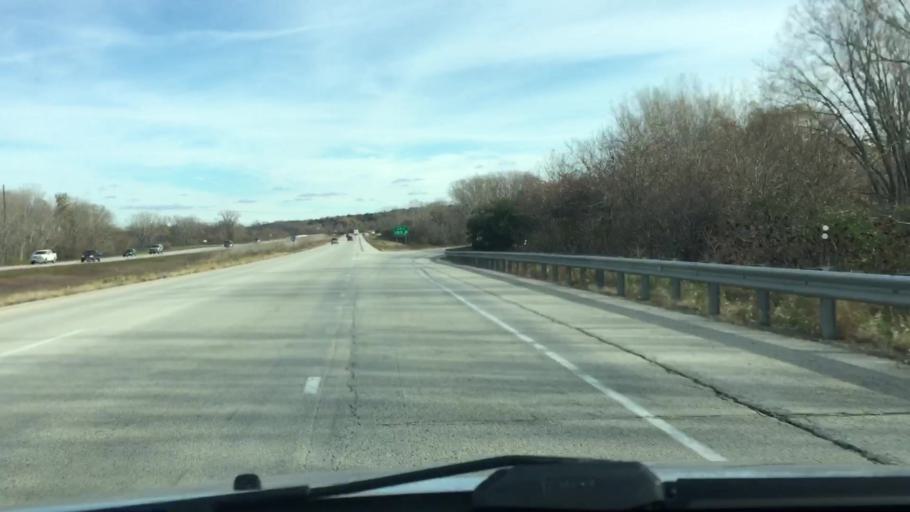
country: US
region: Wisconsin
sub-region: Brown County
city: Green Bay
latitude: 44.5195
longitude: -87.9644
